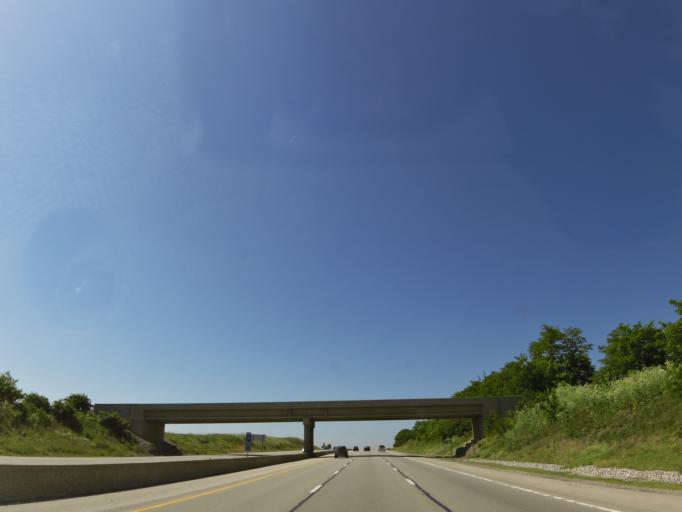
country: US
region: Kentucky
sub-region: Madison County
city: Berea
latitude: 37.6428
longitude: -84.3150
